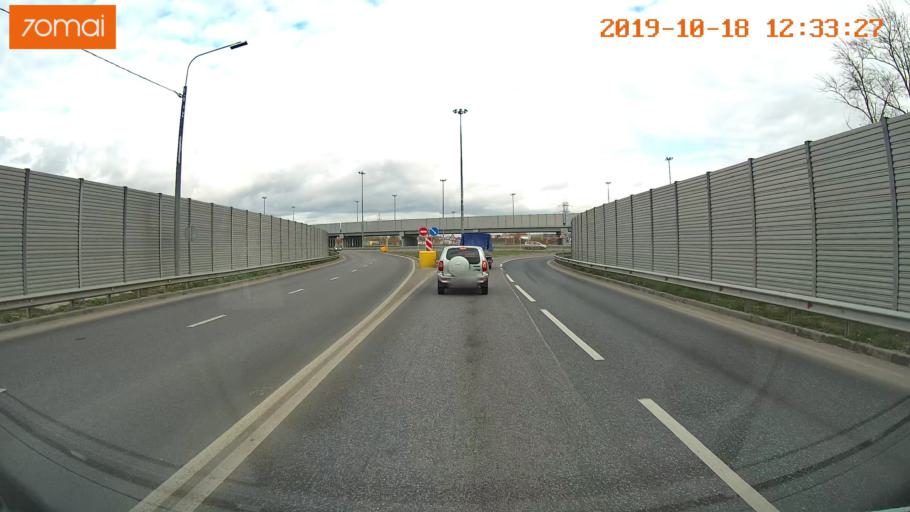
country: RU
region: Rjazan
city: Ryazan'
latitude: 54.6084
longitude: 39.6383
